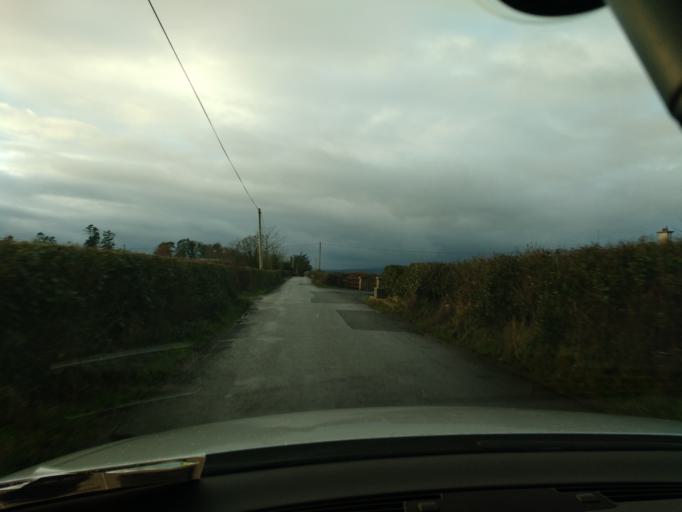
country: IE
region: Munster
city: Thurles
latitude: 52.6343
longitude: -7.8198
